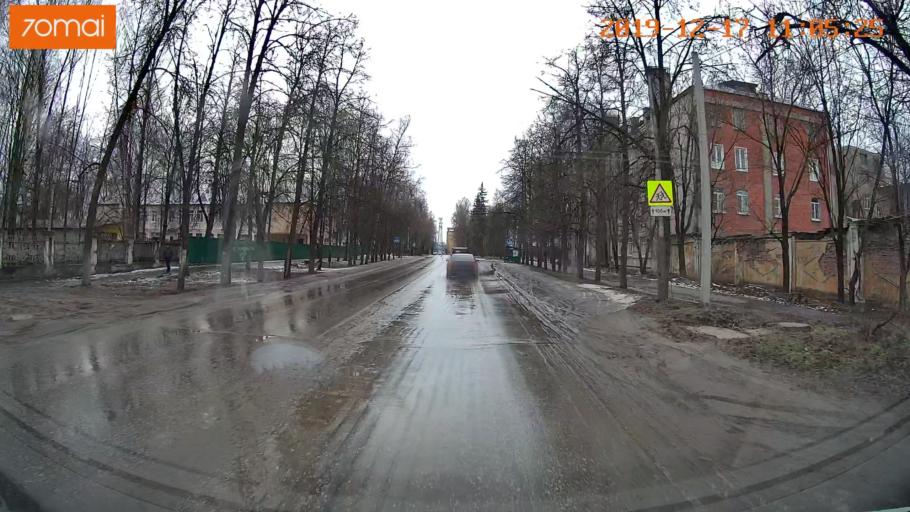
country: RU
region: Vladimir
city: Gus'-Khrustal'nyy
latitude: 55.6212
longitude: 40.6431
